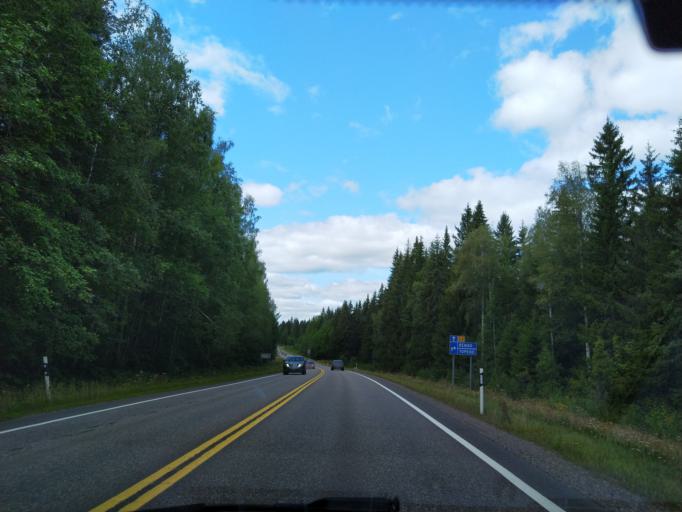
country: FI
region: Haeme
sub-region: Haemeenlinna
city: Renko
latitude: 60.7603
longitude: 24.2897
